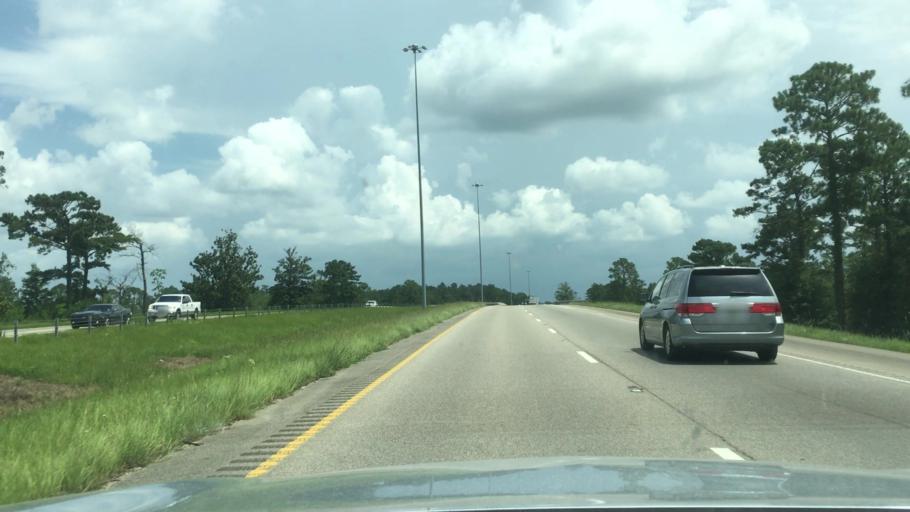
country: US
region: Mississippi
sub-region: Pearl River County
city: Picayune
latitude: 30.5156
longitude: -89.6642
